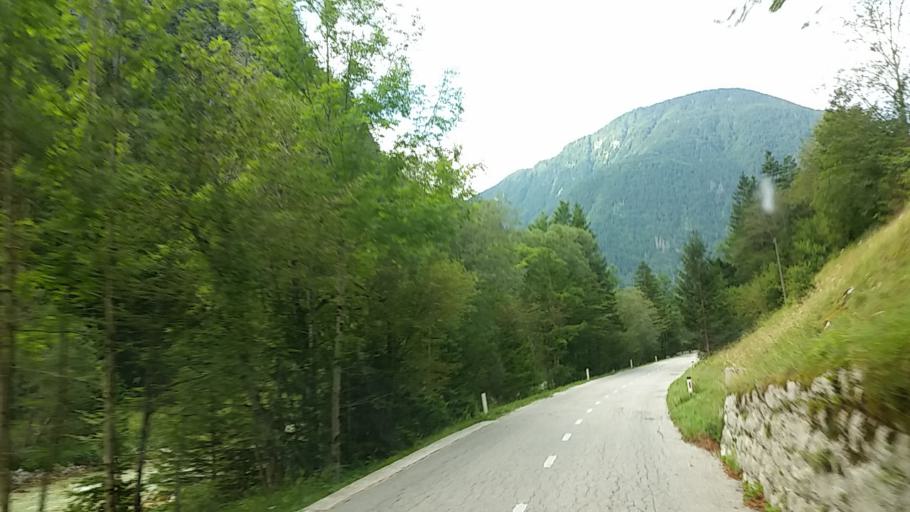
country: SI
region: Kranjska Gora
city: Kranjska Gora
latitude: 46.3511
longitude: 13.6930
